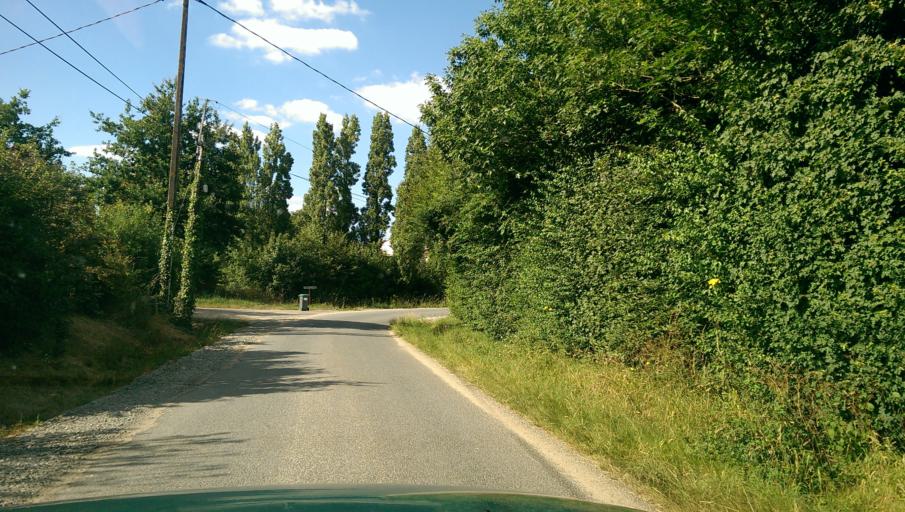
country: FR
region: Pays de la Loire
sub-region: Departement de la Loire-Atlantique
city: Vieillevigne
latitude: 46.9872
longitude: -1.4026
